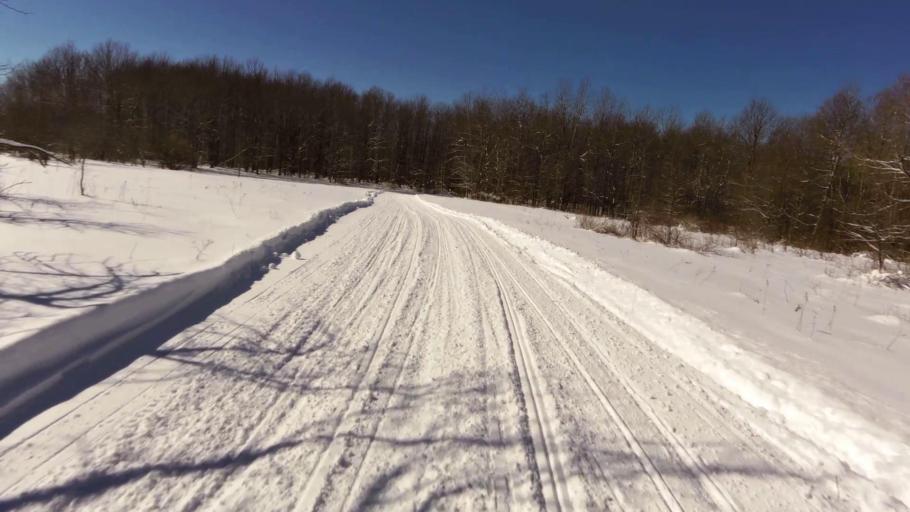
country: US
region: New York
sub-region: Chautauqua County
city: Mayville
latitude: 42.2236
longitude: -79.4003
